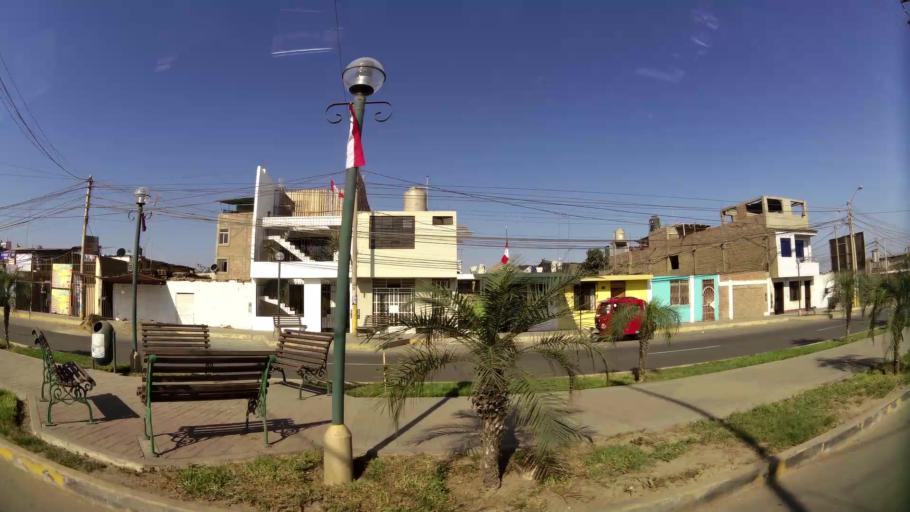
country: PE
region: Ica
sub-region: Provincia de Chincha
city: Chincha Alta
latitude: -13.3999
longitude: -76.1285
